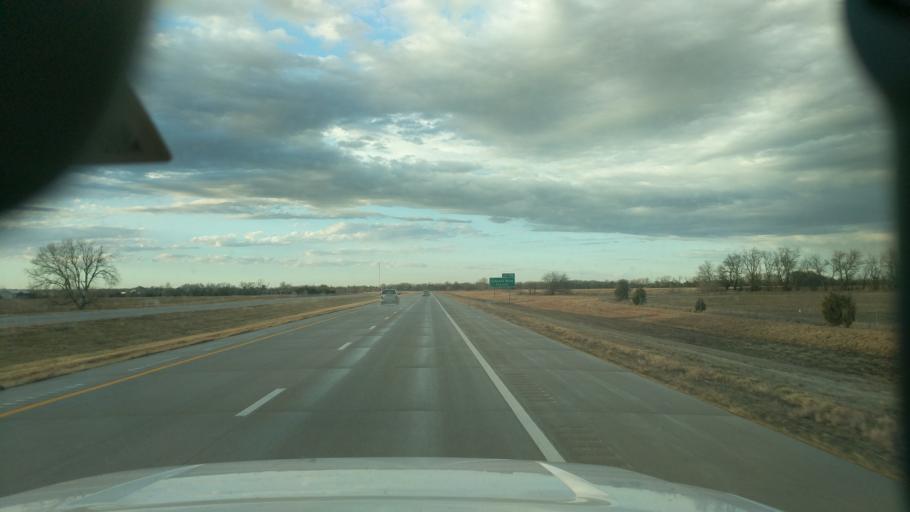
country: US
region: Kansas
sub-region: Harvey County
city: Hesston
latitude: 38.1281
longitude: -97.3993
